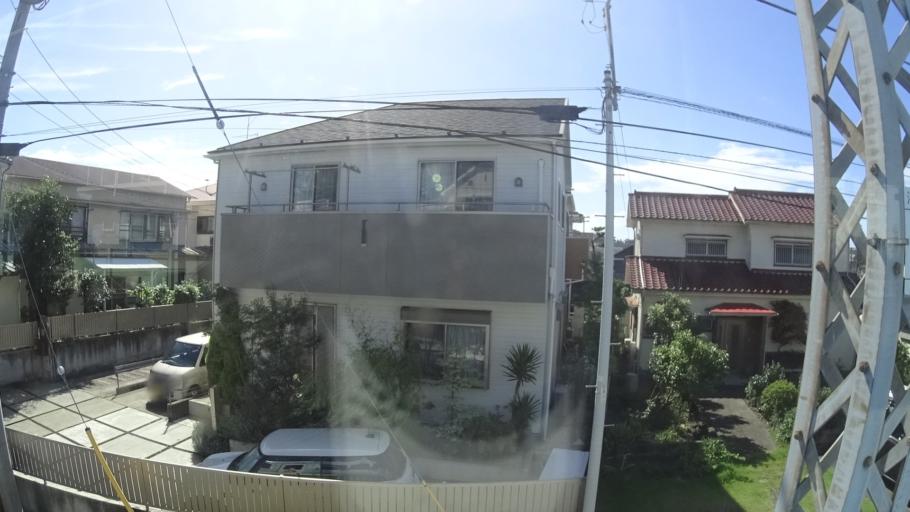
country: JP
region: Kanagawa
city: Fujisawa
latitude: 35.3211
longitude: 139.4826
